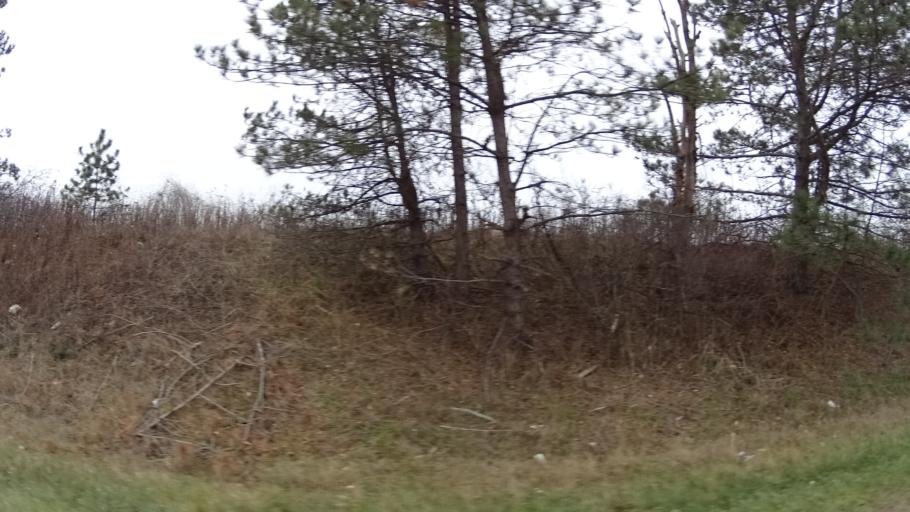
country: US
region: Ohio
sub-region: Lorain County
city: Wellington
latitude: 41.1695
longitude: -82.2718
